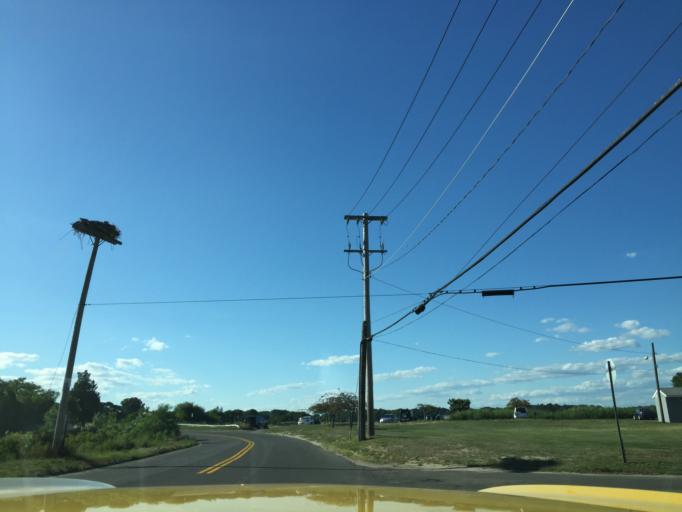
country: US
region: New York
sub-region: Suffolk County
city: Southold
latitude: 41.0508
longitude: -72.4132
